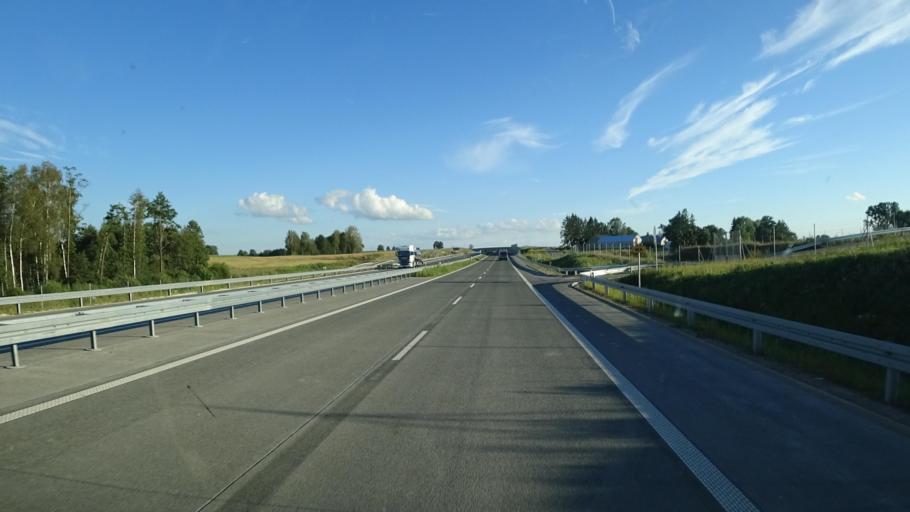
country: PL
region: Podlasie
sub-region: Powiat suwalski
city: Raczki
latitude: 53.9484
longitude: 22.7661
